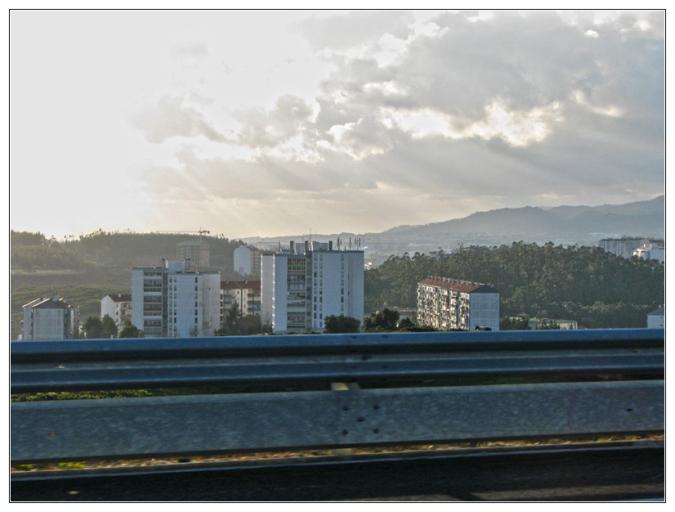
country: PT
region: Lisbon
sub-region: Sintra
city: Cacem
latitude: 38.7870
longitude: -9.2985
